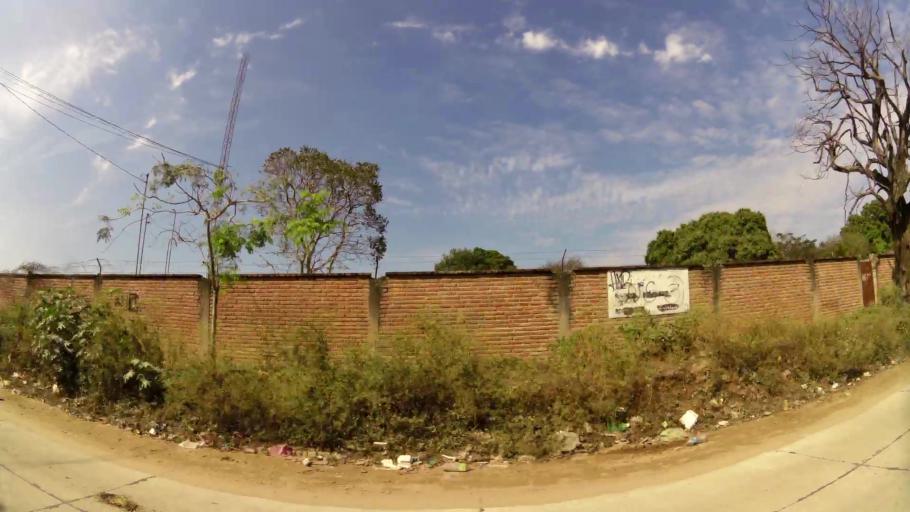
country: BO
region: Santa Cruz
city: Santa Cruz de la Sierra
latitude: -17.7201
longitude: -63.1543
